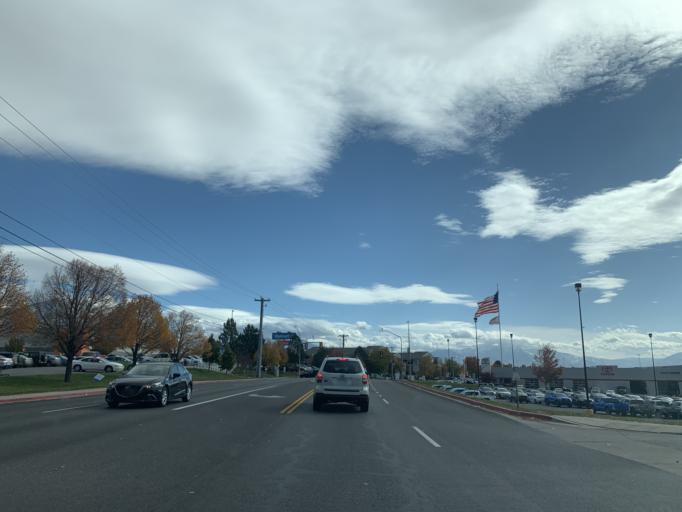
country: US
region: Utah
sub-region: Utah County
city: Orem
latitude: 40.2733
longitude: -111.7127
